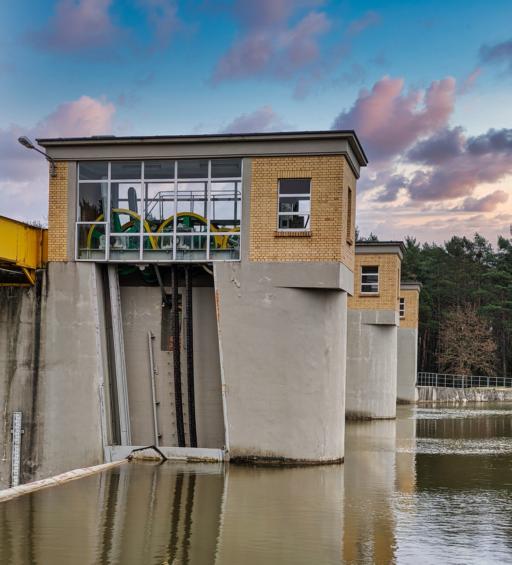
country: PL
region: Lubusz
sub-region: Powiat zielonogorski
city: Nowogrod Bobrzanski
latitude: 51.8313
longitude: 15.2028
